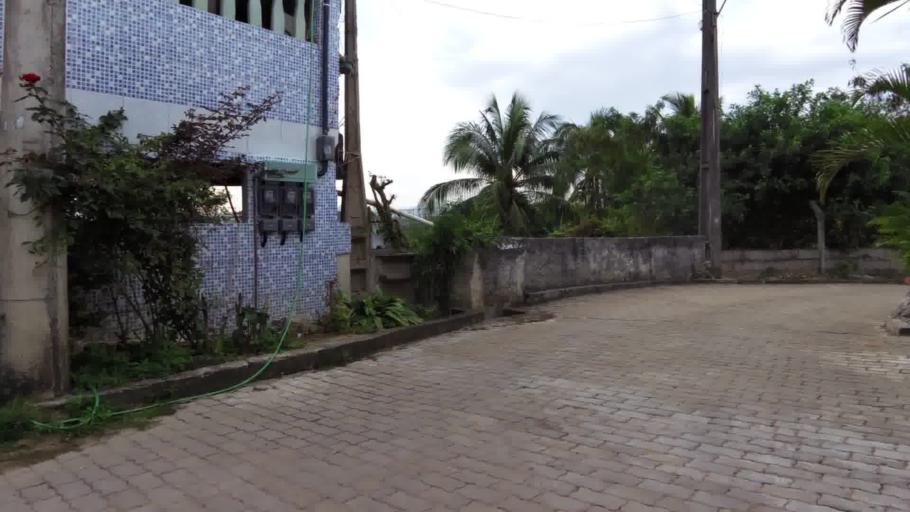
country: BR
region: Espirito Santo
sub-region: Piuma
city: Piuma
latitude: -20.8321
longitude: -40.7280
